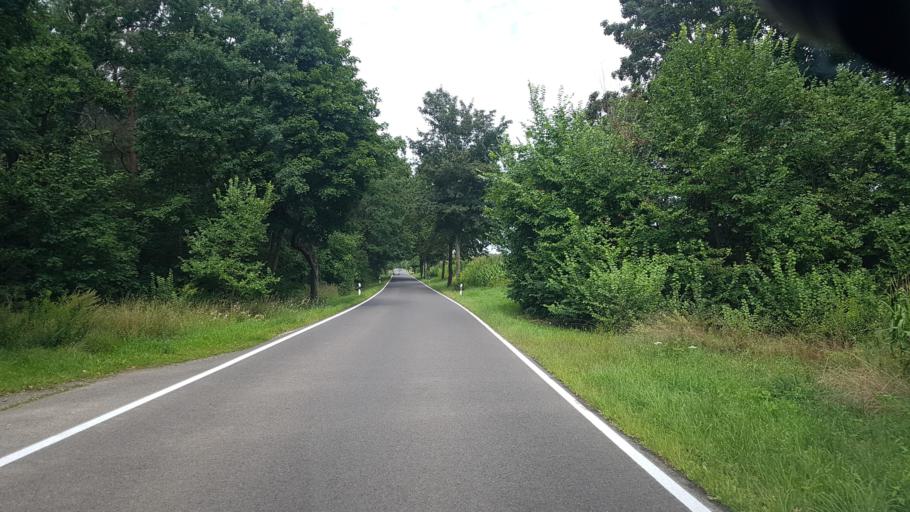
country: DE
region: Brandenburg
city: Spremberg
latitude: 51.5902
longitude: 14.3483
